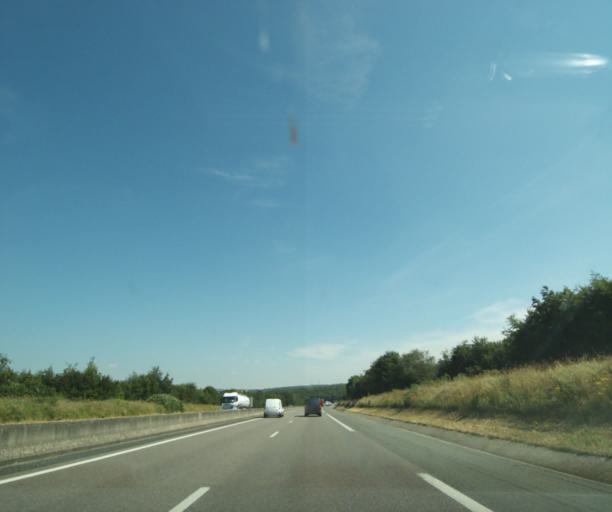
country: FR
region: Lorraine
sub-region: Departement de Meurthe-et-Moselle
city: Colombey-les-Belles
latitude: 48.4534
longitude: 5.8682
